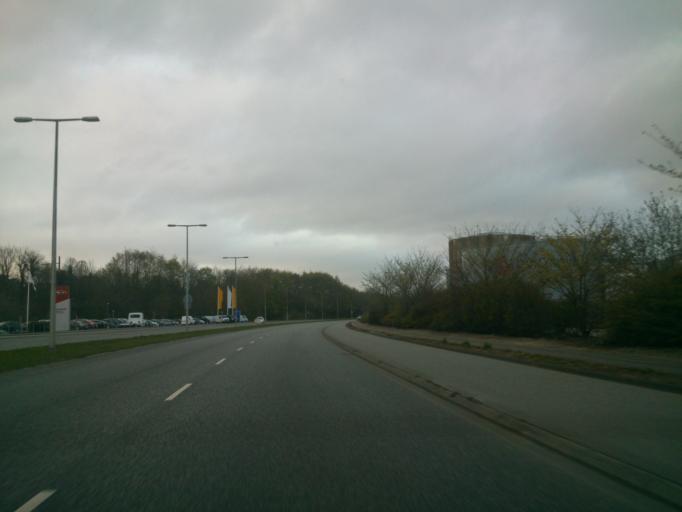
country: DK
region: South Denmark
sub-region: Fredericia Kommune
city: Fredericia
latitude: 55.5573
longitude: 9.7296
